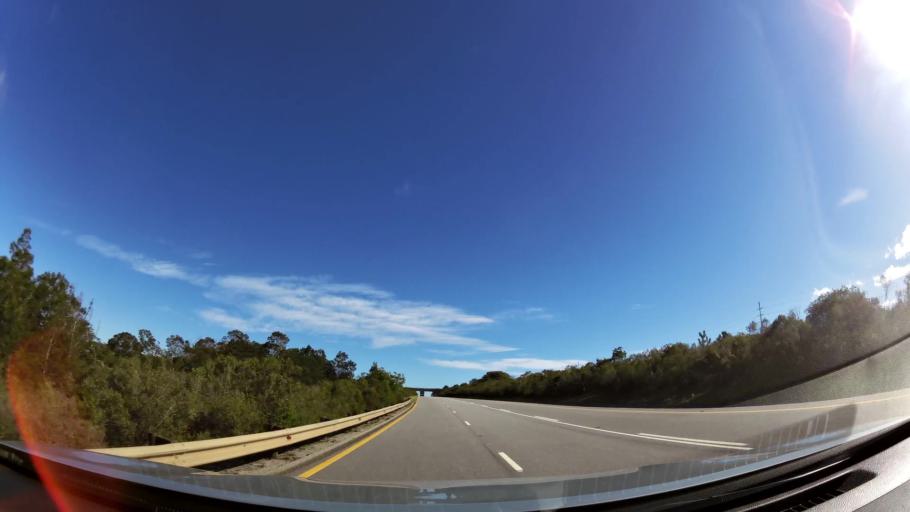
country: ZA
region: Eastern Cape
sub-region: Cacadu District Municipality
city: Kruisfontein
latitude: -34.0171
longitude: 24.6244
